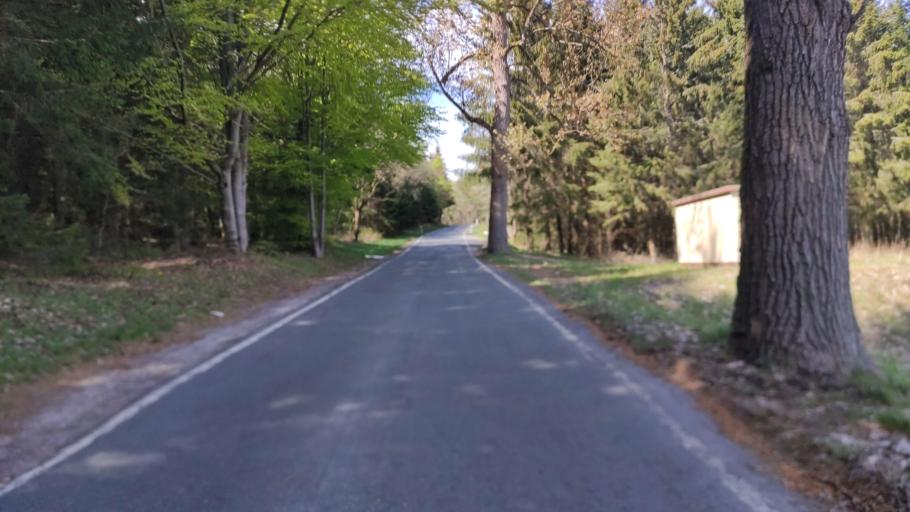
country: DE
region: Thuringia
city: Leutenberg
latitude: 50.5007
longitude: 11.4596
